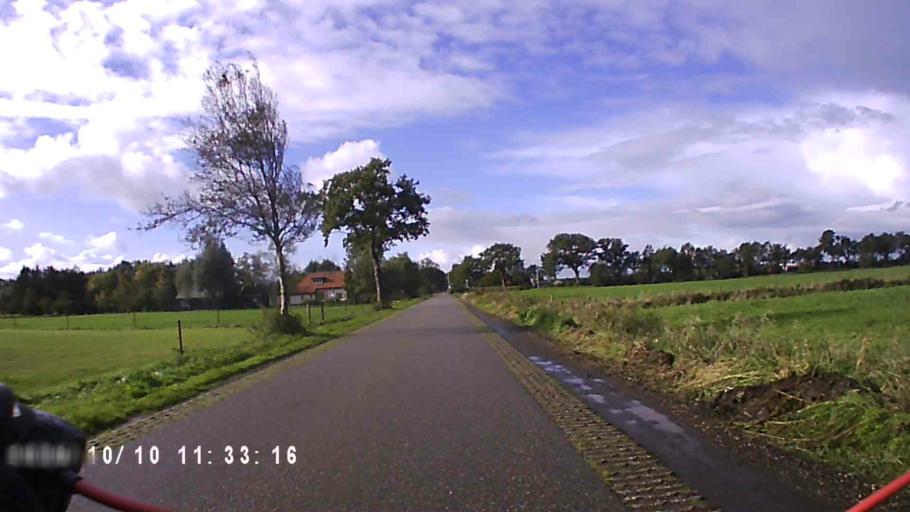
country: NL
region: Friesland
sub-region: Gemeente Smallingerland
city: Drachten
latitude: 53.0808
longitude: 6.1307
